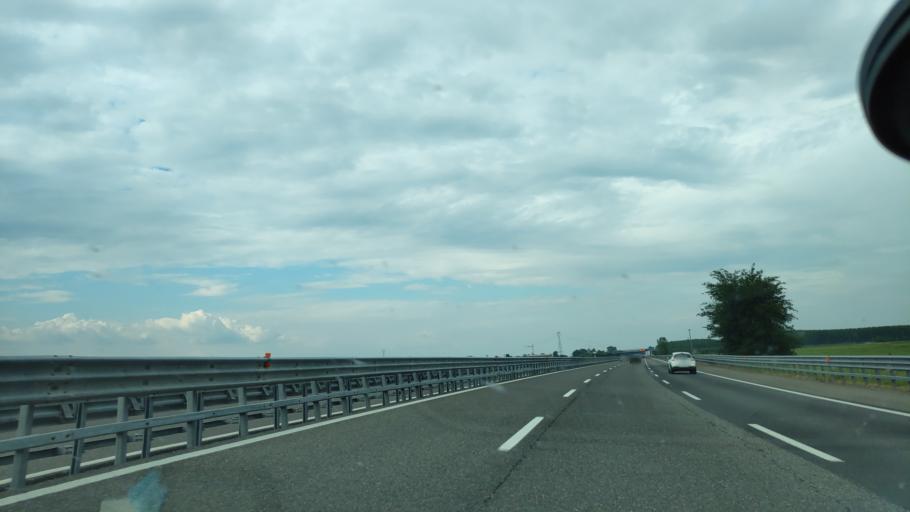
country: IT
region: Lombardy
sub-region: Provincia di Pavia
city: Corana
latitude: 45.0563
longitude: 8.9539
